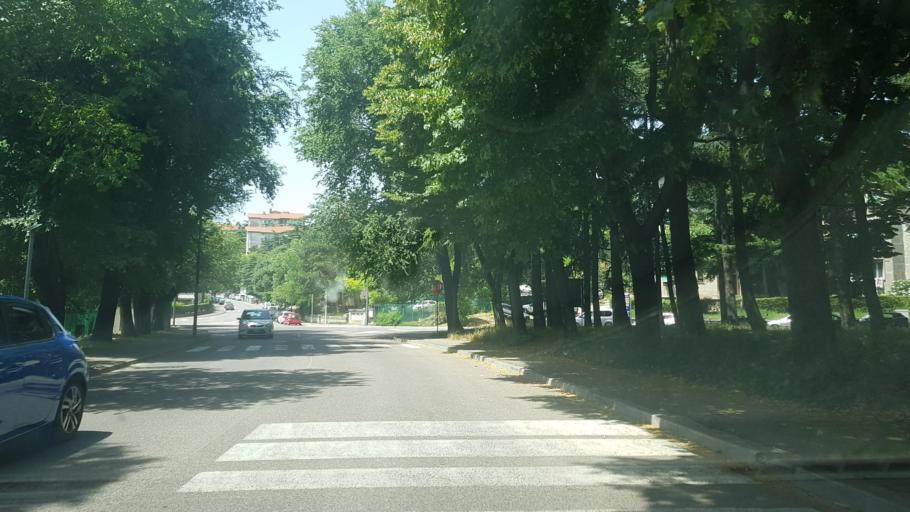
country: IT
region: Friuli Venezia Giulia
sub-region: Provincia di Trieste
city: Domio
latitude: 45.6184
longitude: 13.8209
